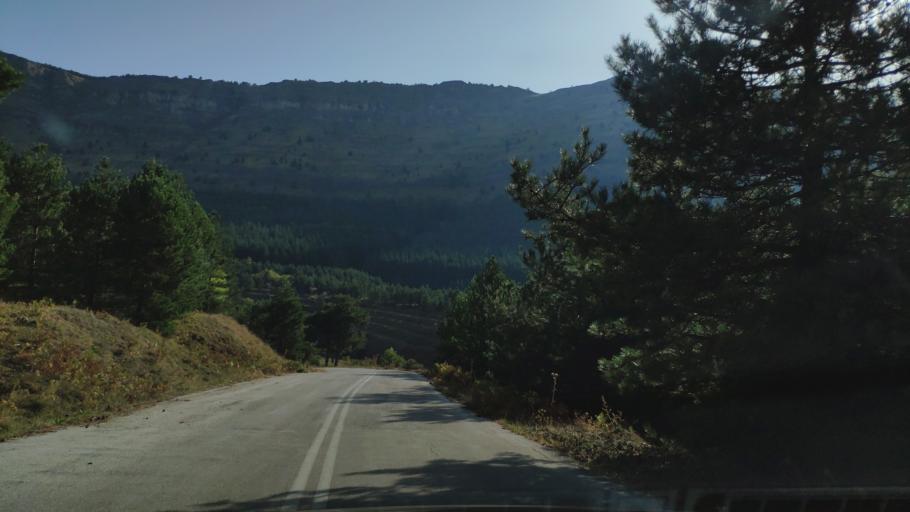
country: GR
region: West Greece
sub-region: Nomos Achaias
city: Aiyira
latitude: 38.0498
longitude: 22.3854
